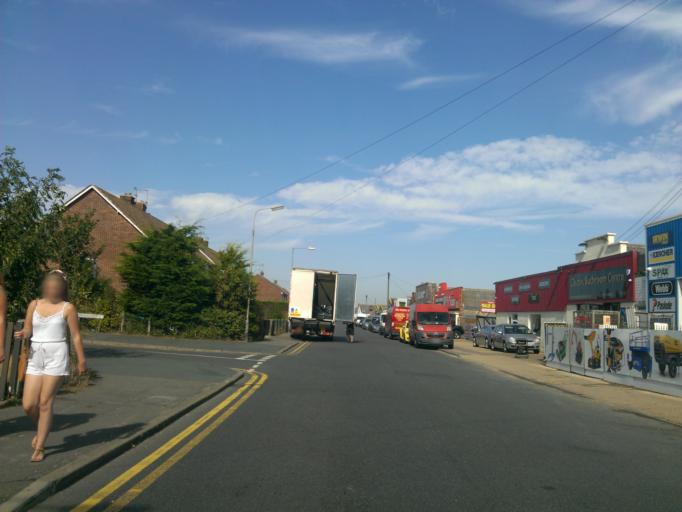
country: GB
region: England
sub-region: Essex
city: Clacton-on-Sea
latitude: 51.7977
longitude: 1.1566
